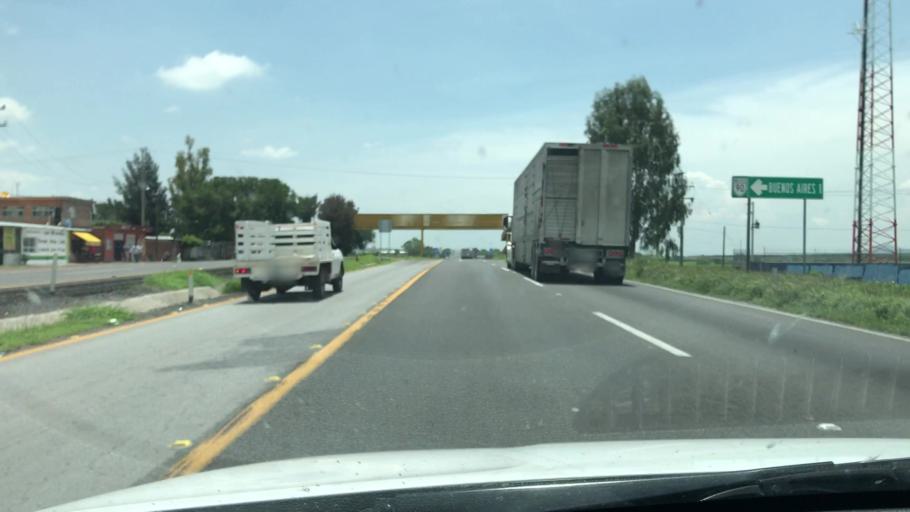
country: MX
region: Guanajuato
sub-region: Penjamo
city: Mezquite de Luna
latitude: 20.3791
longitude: -101.8373
